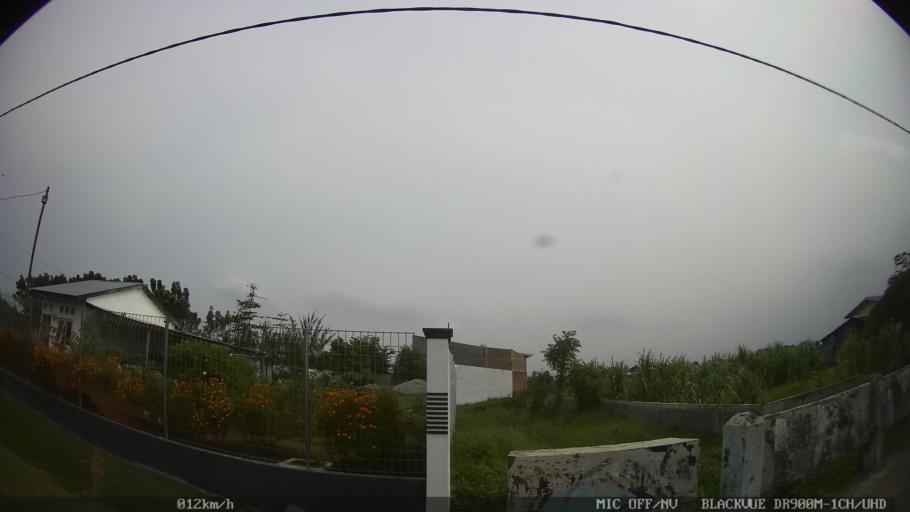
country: ID
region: North Sumatra
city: Medan
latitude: 3.5732
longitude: 98.7547
